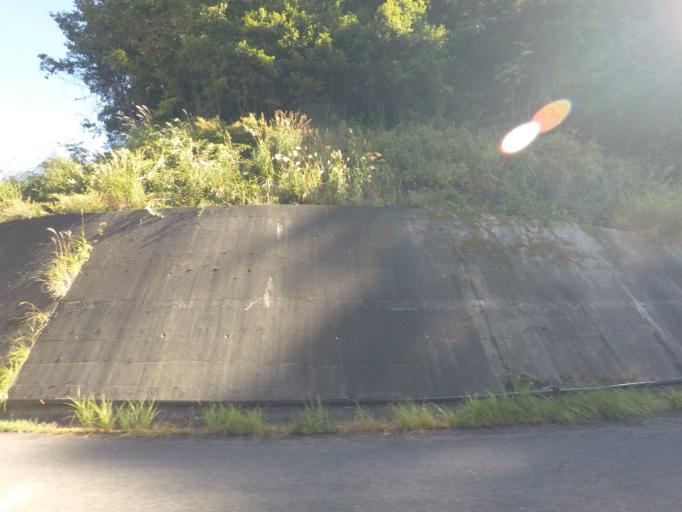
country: JP
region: Nagano
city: Tatsuno
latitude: 35.9692
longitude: 137.7736
